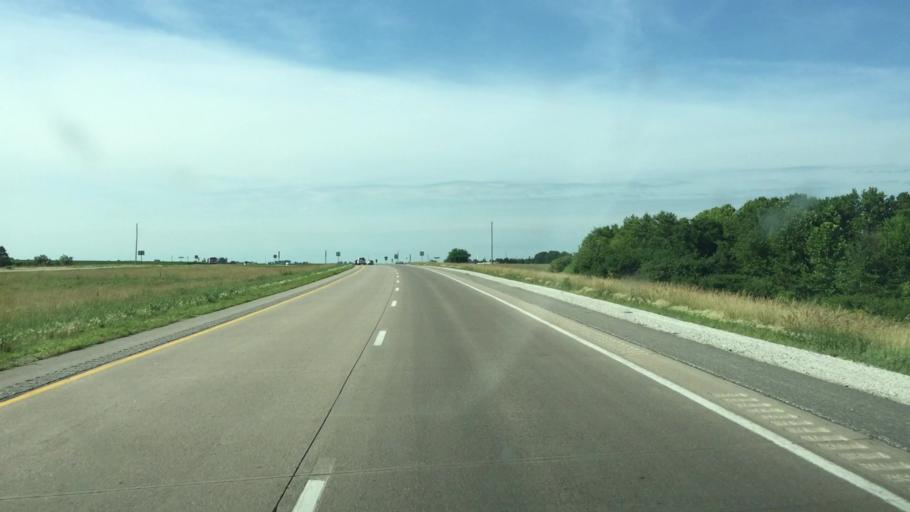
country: US
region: Iowa
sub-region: Henry County
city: Winfield
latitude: 41.1650
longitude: -91.5423
